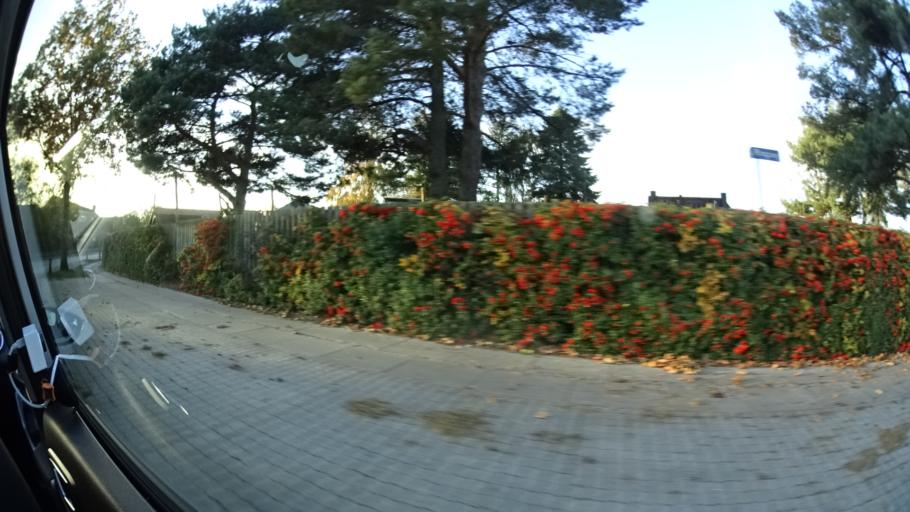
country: DK
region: South Denmark
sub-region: Odense Kommune
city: Odense
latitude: 55.3871
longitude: 10.4209
